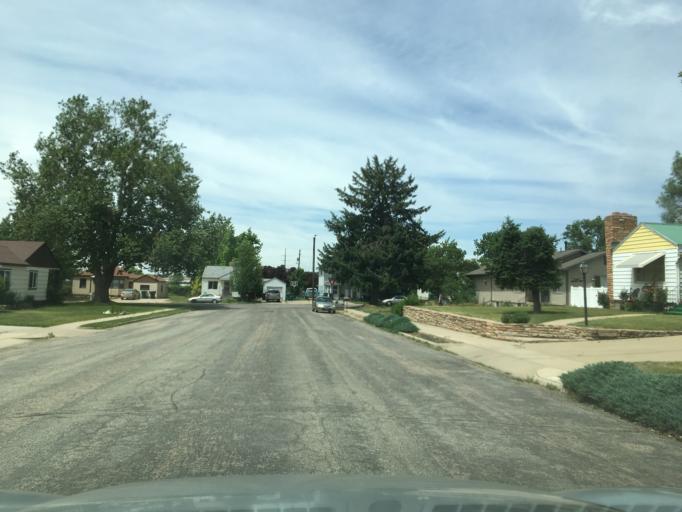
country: US
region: Utah
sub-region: Davis County
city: Layton
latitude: 41.0610
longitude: -111.9539
